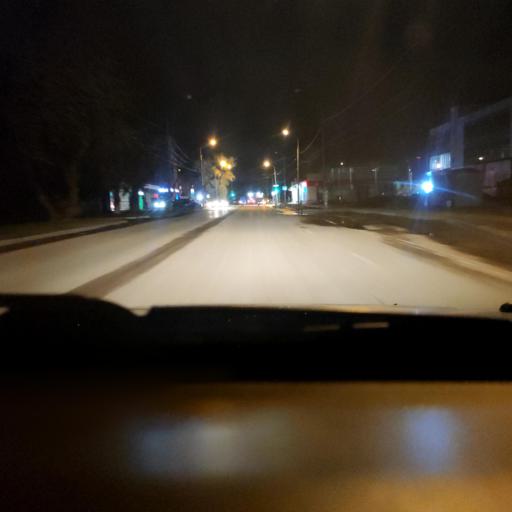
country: RU
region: Perm
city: Perm
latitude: 57.9661
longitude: 56.2418
